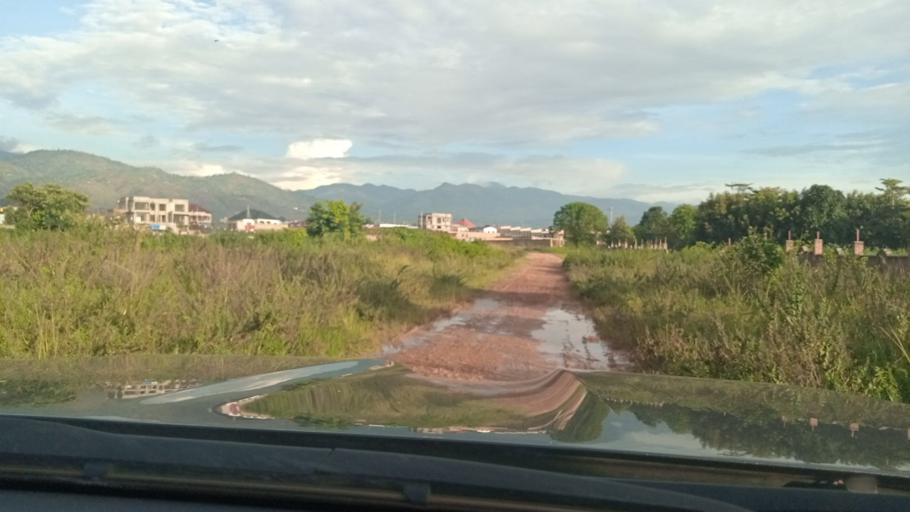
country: BI
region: Bujumbura Mairie
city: Bujumbura
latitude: -3.4442
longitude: 29.3448
